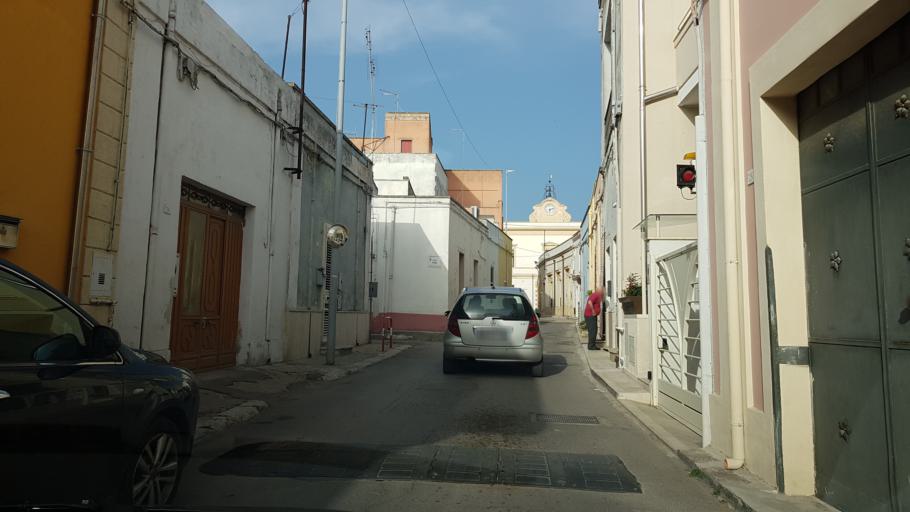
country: IT
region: Apulia
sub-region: Provincia di Brindisi
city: San Donaci
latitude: 40.4463
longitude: 17.9203
